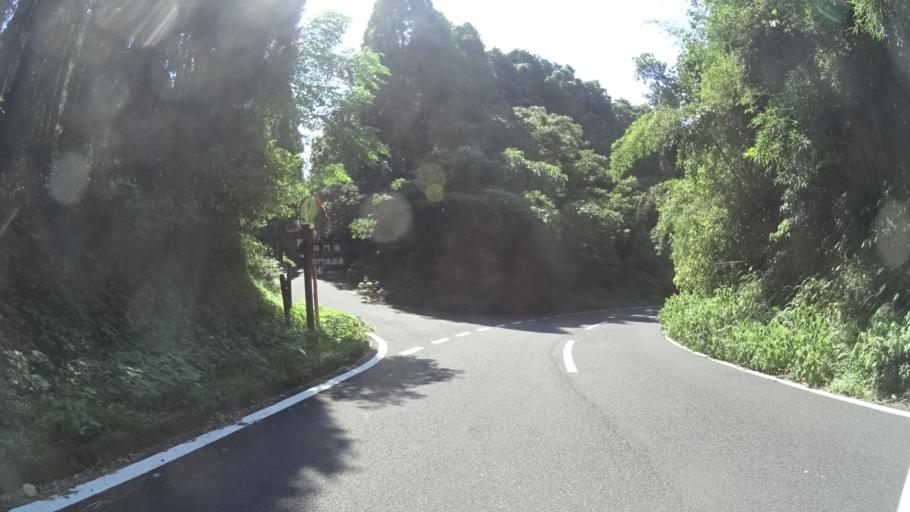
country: JP
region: Kagoshima
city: Kajiki
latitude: 31.7543
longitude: 130.6695
